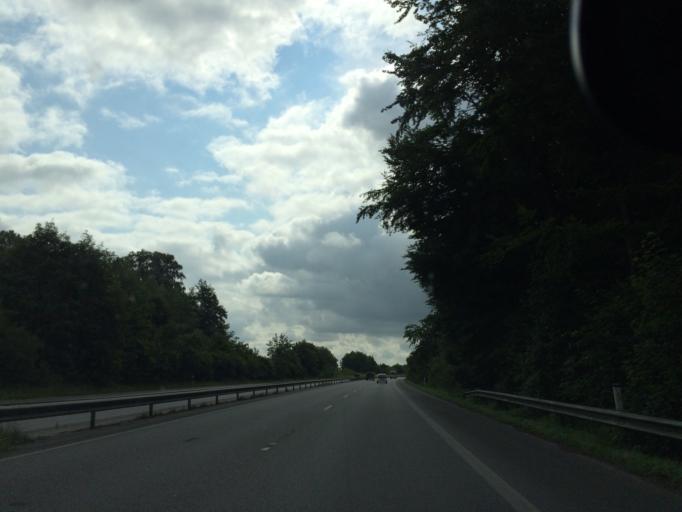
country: DE
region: Schleswig-Holstein
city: Tuttendorf
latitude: 54.3910
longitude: 10.0235
